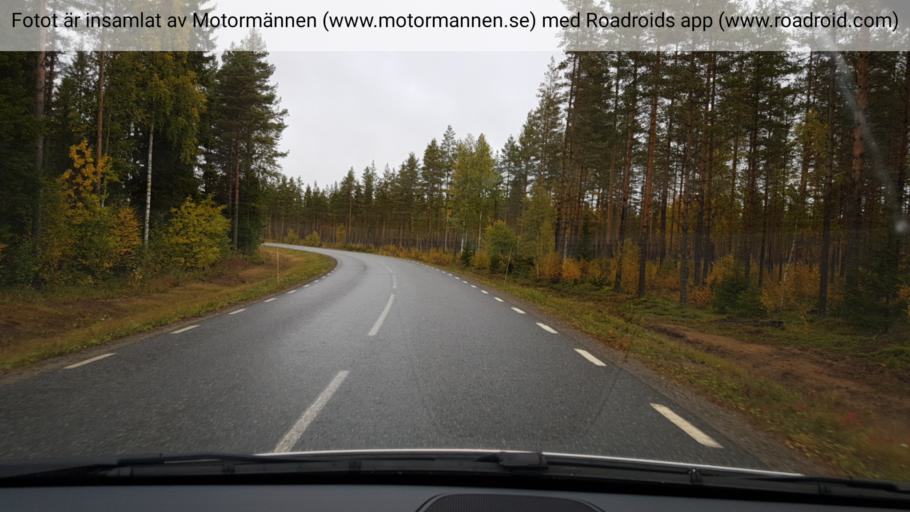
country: SE
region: Vaesterbotten
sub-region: Umea Kommun
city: Ersmark
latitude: 64.1408
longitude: 20.3813
